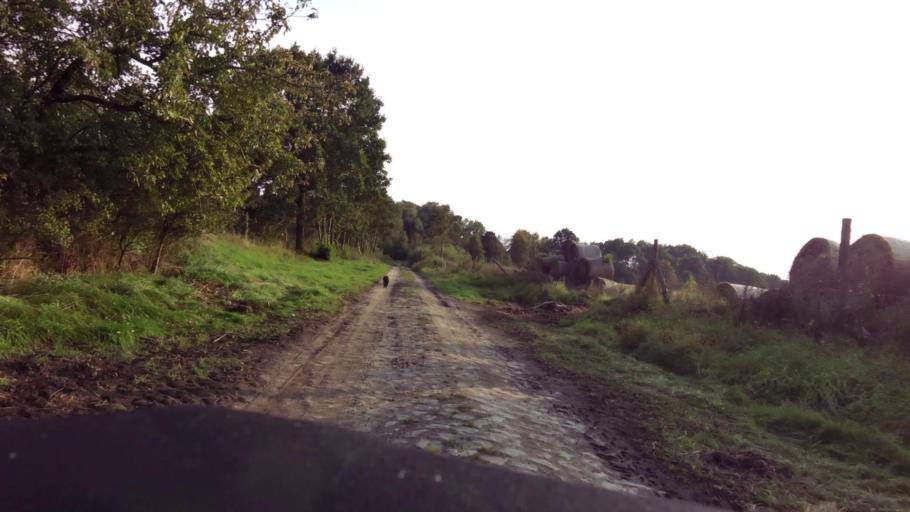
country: PL
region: West Pomeranian Voivodeship
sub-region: Powiat stargardzki
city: Suchan
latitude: 53.3337
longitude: 15.3645
